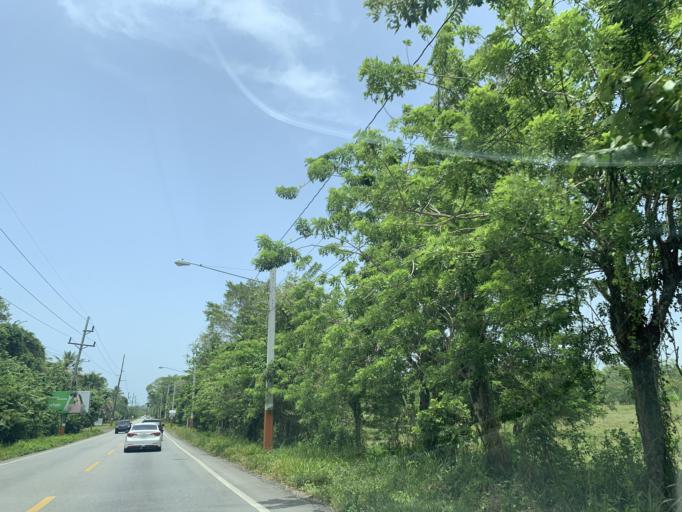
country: DO
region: Puerto Plata
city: Cabarete
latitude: 19.7773
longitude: -70.4726
